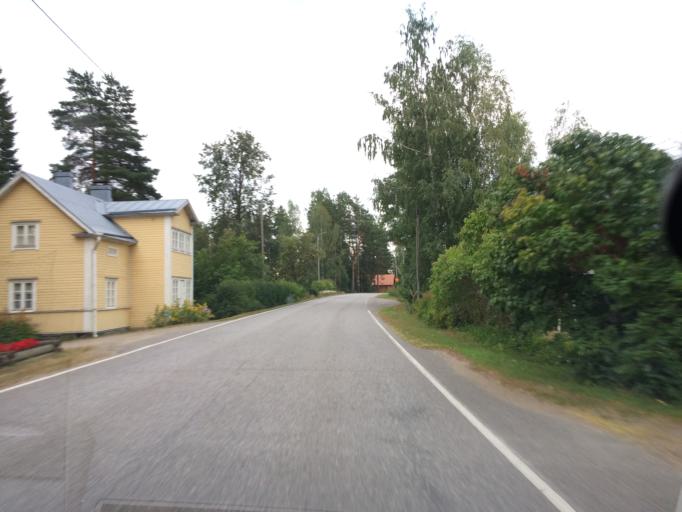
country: FI
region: Haeme
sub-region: Haemeenlinna
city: Tuulos
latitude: 61.2184
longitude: 24.7289
